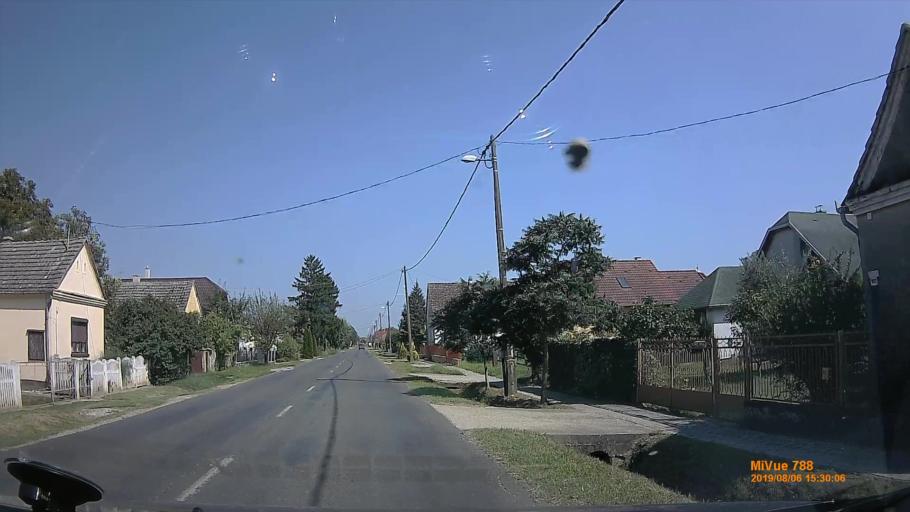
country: HR
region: Koprivnicko-Krizevacka
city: Sigetec
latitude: 46.2398
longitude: 16.9857
